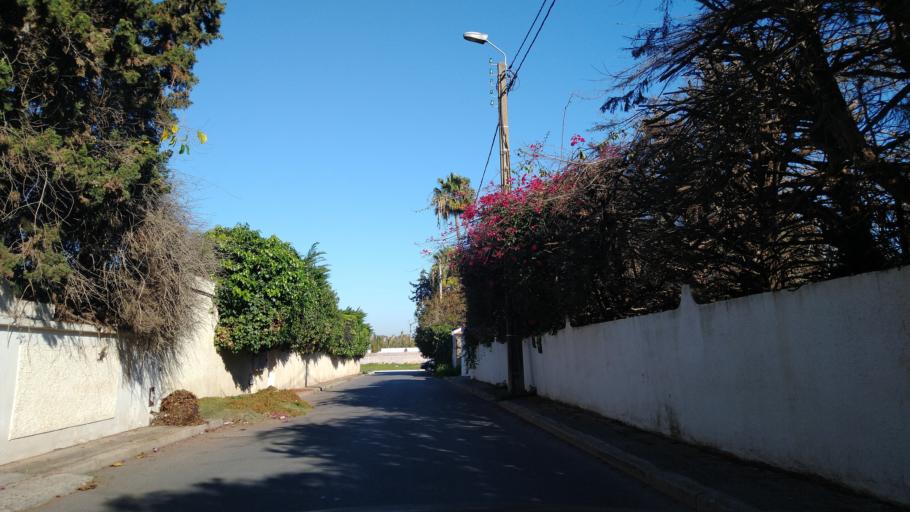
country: MA
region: Rabat-Sale-Zemmour-Zaer
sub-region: Rabat
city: Rabat
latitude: 33.9596
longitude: -6.8377
